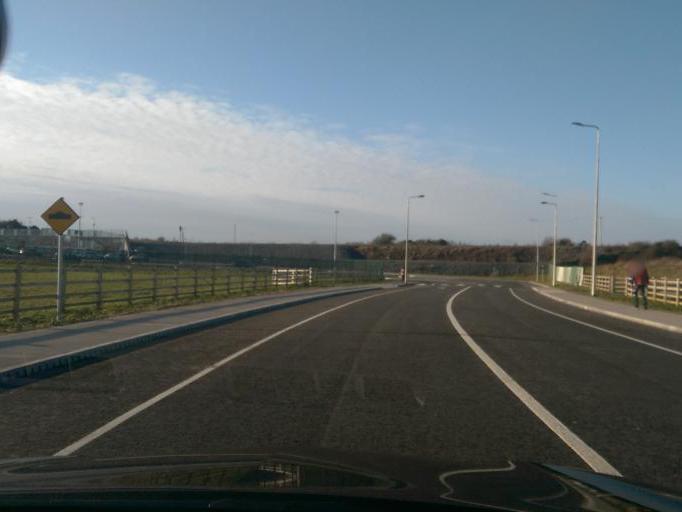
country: IE
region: Connaught
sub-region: County Galway
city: Oranmore
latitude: 53.2746
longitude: -8.9451
